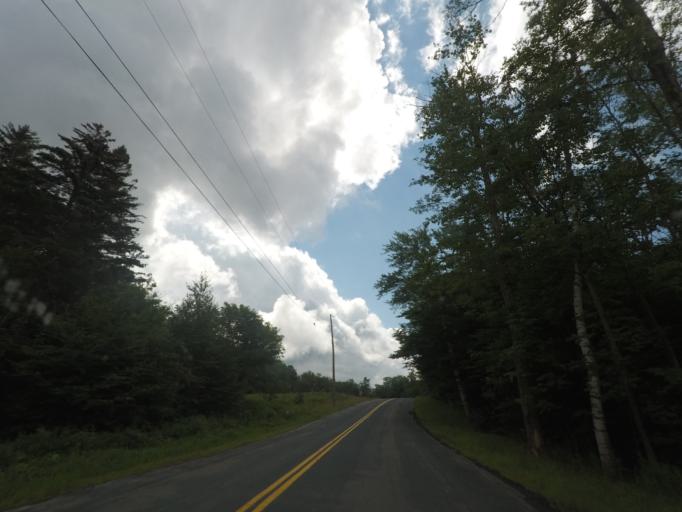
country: US
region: New York
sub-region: Rensselaer County
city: Averill Park
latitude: 42.6640
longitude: -73.4147
